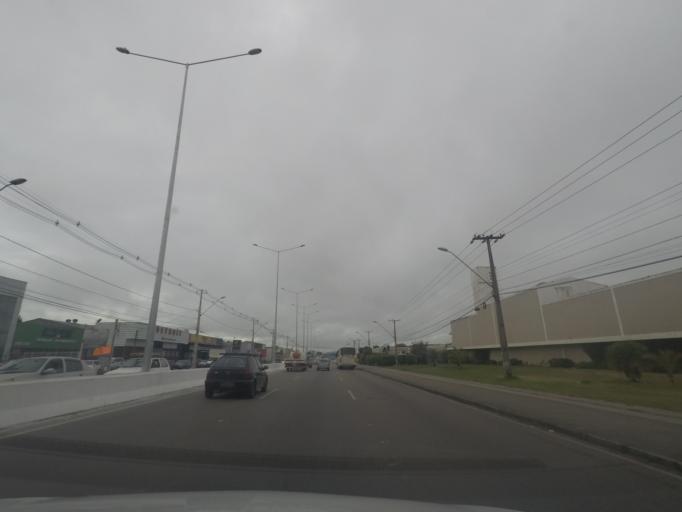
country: BR
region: Parana
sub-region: Pinhais
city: Pinhais
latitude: -25.4341
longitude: -49.1781
